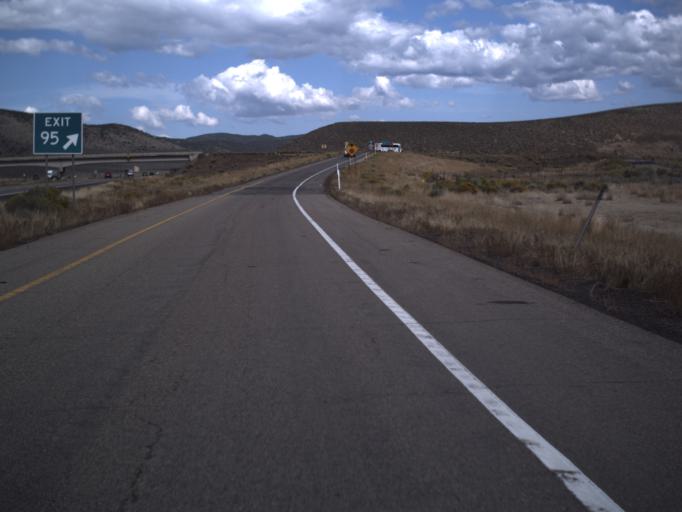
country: US
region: Utah
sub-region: Beaver County
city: Beaver
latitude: 38.0679
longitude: -112.6902
